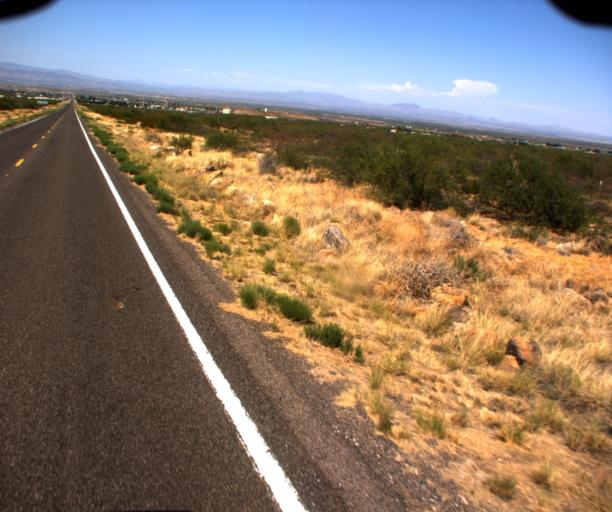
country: US
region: Arizona
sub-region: Graham County
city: Swift Trail Junction
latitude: 32.7061
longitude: -109.7381
